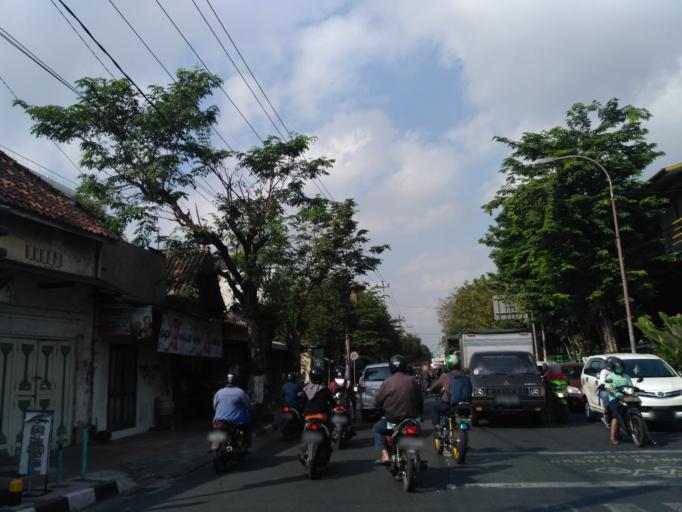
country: ID
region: Daerah Istimewa Yogyakarta
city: Yogyakarta
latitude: -7.8013
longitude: 110.3565
